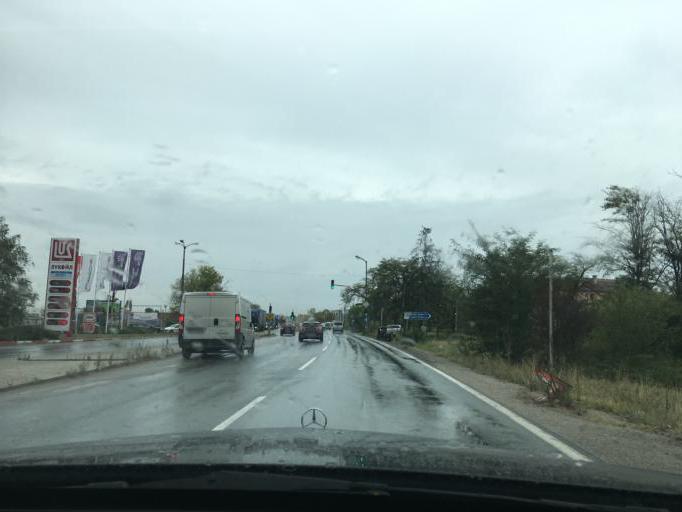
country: BG
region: Sofiya
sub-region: Obshtina Bozhurishte
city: Bozhurishte
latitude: 42.7460
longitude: 23.2284
